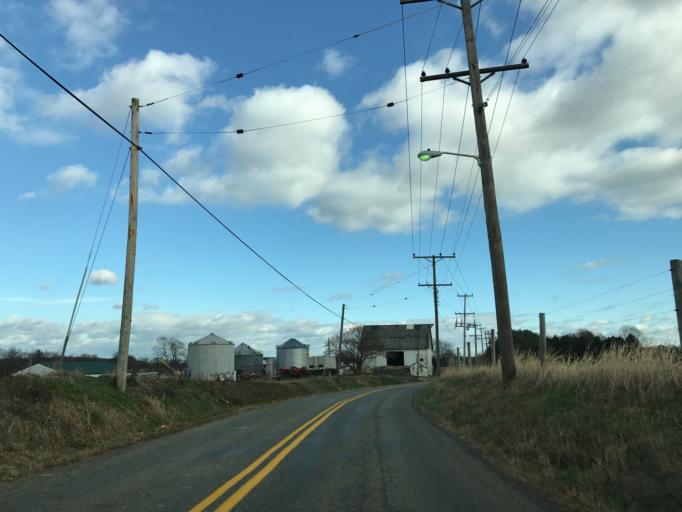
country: US
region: Maryland
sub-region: Harford County
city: Jarrettsville
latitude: 39.6353
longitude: -76.5601
